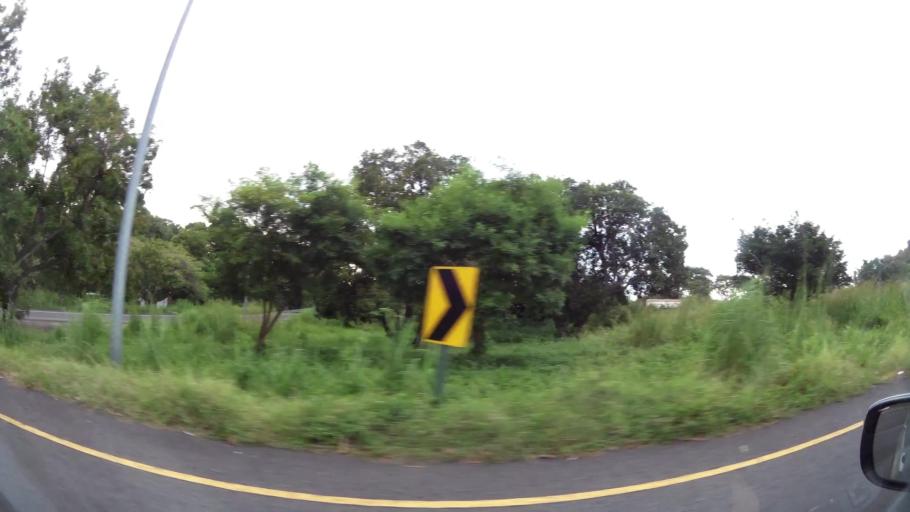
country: CR
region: Alajuela
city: Orotina
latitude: 9.9058
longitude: -84.5221
